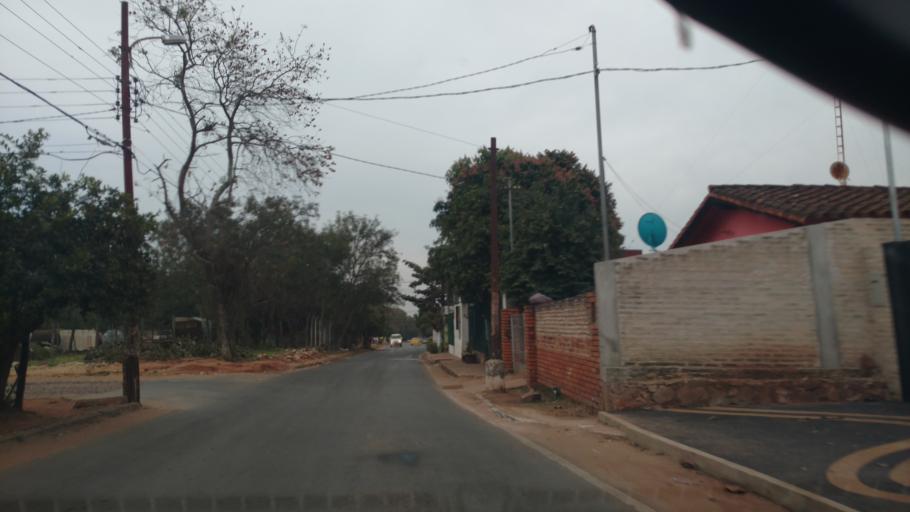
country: PY
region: Central
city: San Lorenzo
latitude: -25.3520
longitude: -57.4806
